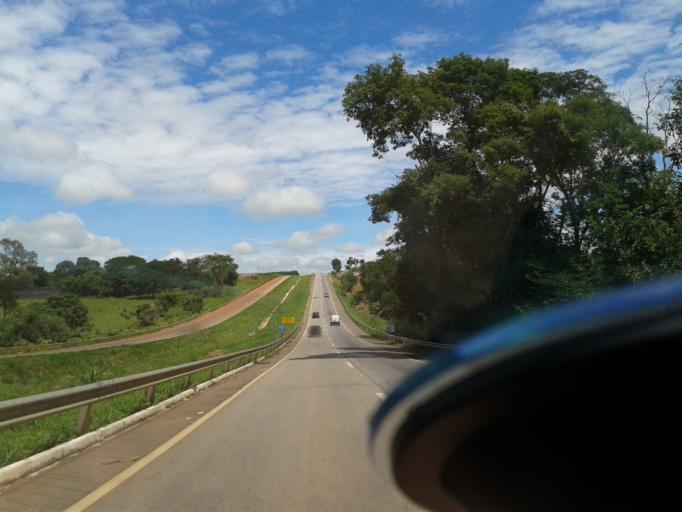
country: BR
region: Goias
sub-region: Inhumas
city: Inhumas
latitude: -16.2985
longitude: -49.5324
